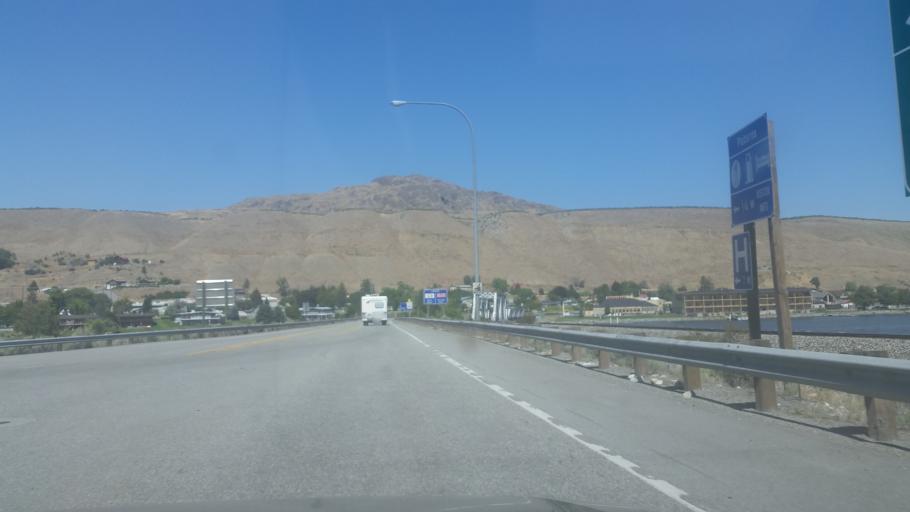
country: US
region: Washington
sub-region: Okanogan County
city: Brewster
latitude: 48.0482
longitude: -119.9011
